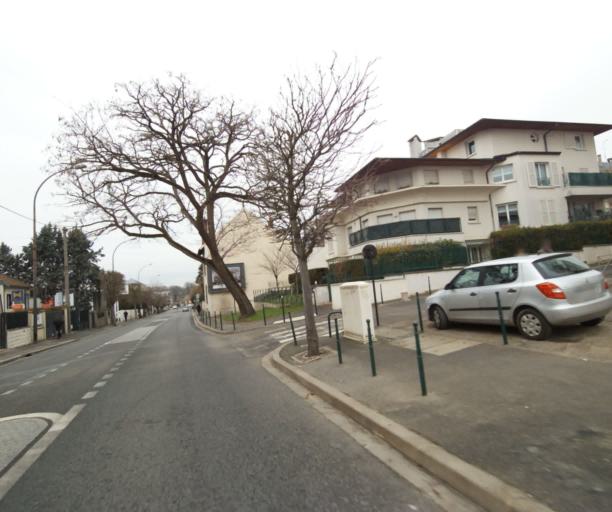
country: FR
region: Ile-de-France
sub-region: Departement des Hauts-de-Seine
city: Rueil-Malmaison
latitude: 48.8684
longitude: 2.1903
